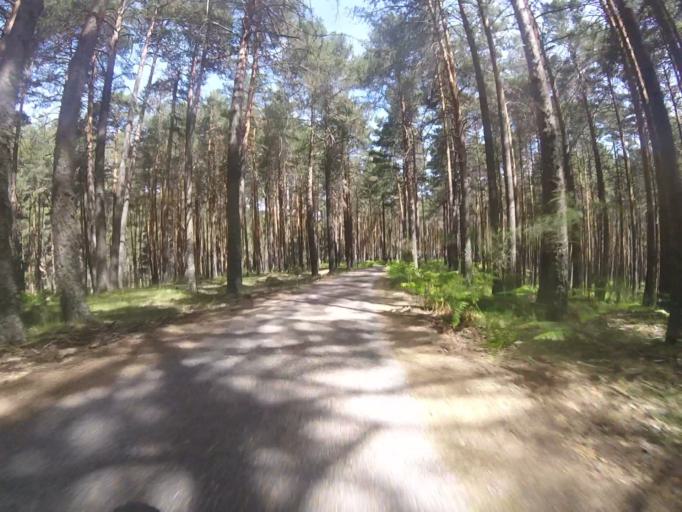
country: ES
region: Madrid
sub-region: Provincia de Madrid
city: Cercedilla
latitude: 40.8159
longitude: -4.0292
